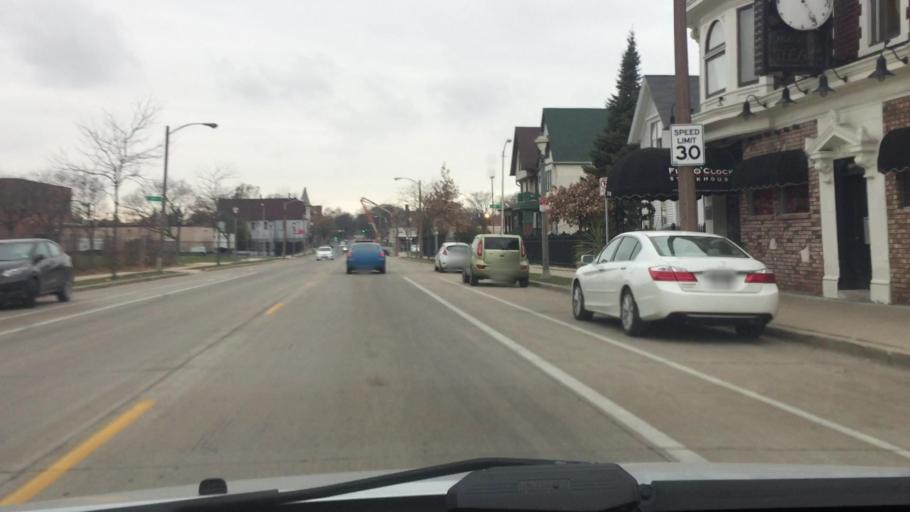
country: US
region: Wisconsin
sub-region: Milwaukee County
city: Milwaukee
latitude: 43.0433
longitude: -87.9433
